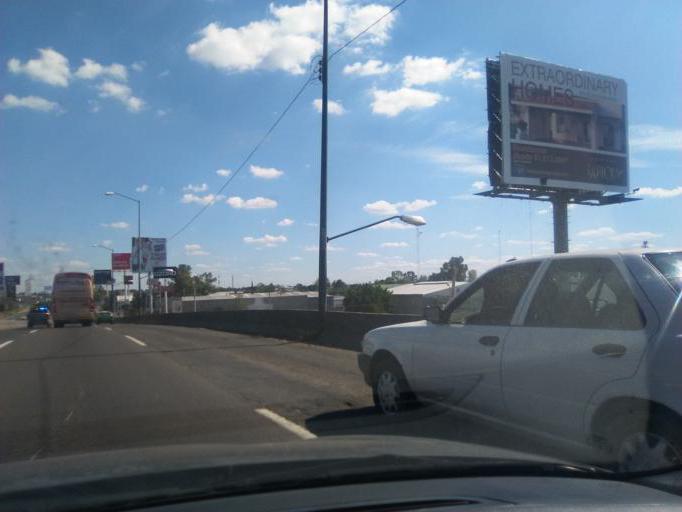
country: MX
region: Guanajuato
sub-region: Leon
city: Fraccionamiento Paraiso Real
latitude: 21.0899
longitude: -101.6203
